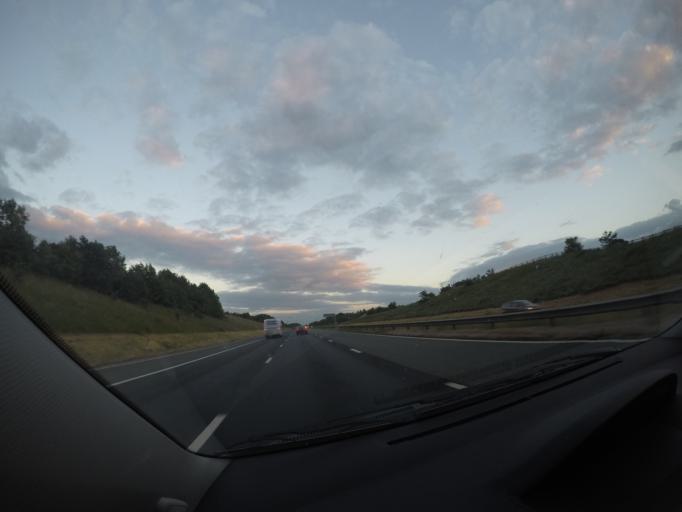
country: GB
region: England
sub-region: North Yorkshire
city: Boroughbridge
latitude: 54.0621
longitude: -1.3905
